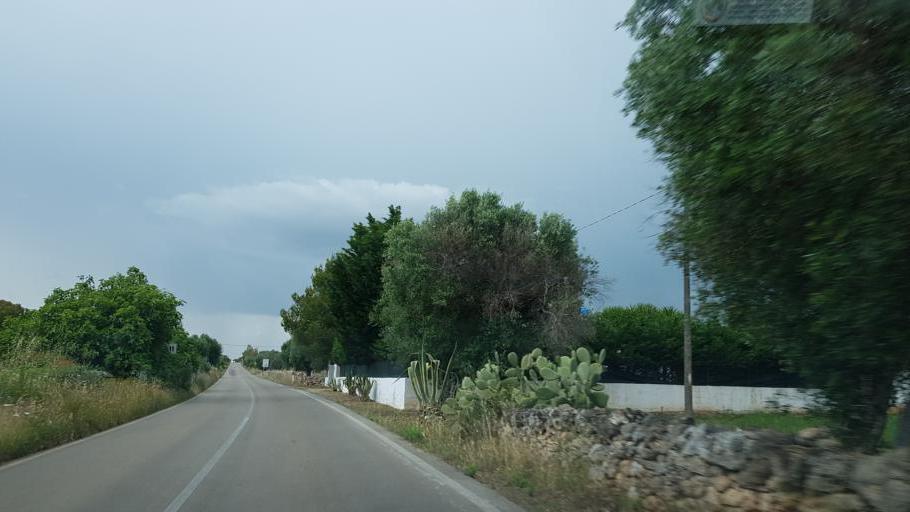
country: IT
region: Apulia
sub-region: Provincia di Lecce
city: Porto Cesareo
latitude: 40.3112
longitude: 17.8632
